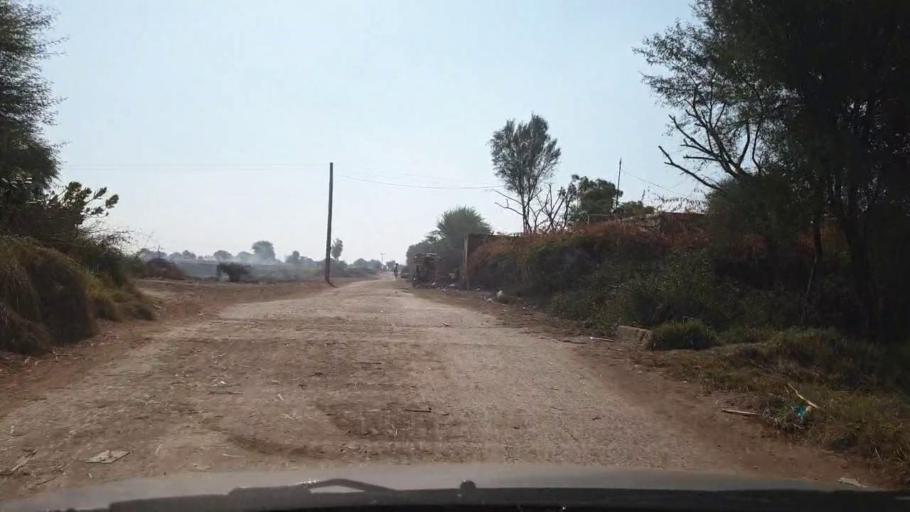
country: PK
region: Sindh
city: Jhol
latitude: 25.9383
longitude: 68.8000
